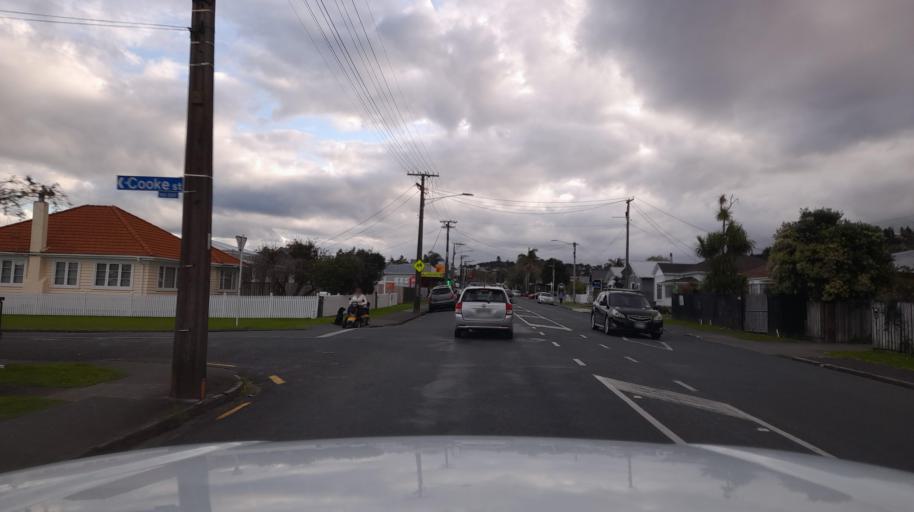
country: NZ
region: Northland
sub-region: Whangarei
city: Whangarei
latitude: -35.7301
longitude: 174.3135
